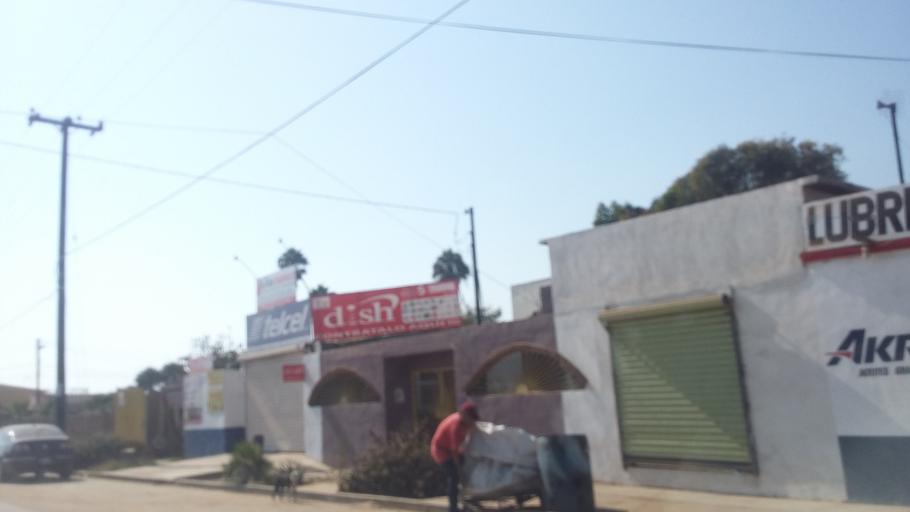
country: MX
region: Baja California
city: Ensenada
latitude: 31.8321
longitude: -116.6056
